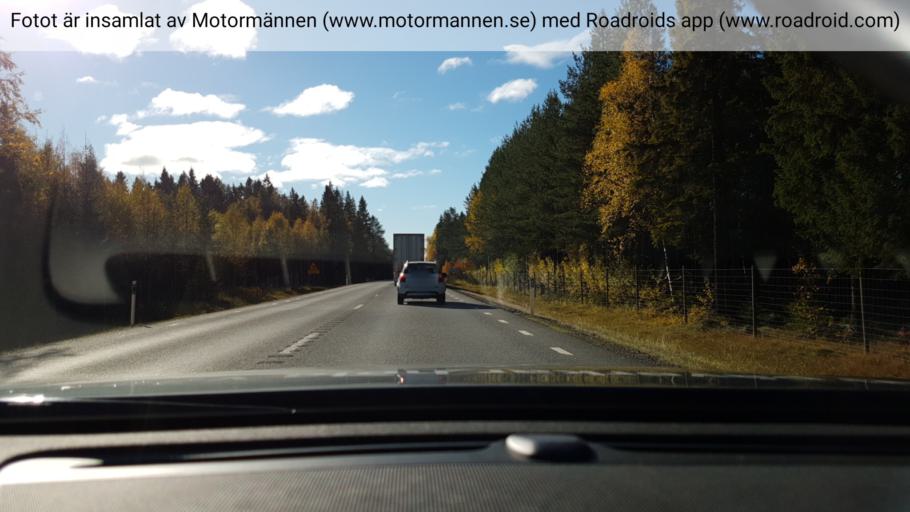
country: SE
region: Vaesterbotten
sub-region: Skelleftea Kommun
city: Burea
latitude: 64.5200
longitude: 21.2586
